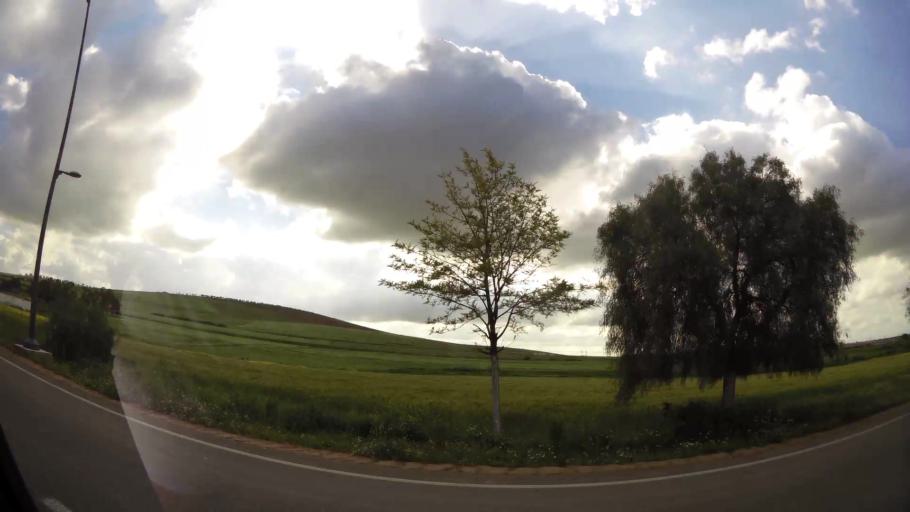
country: MA
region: Chaouia-Ouardigha
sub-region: Settat Province
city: Settat
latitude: 33.0579
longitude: -7.6264
